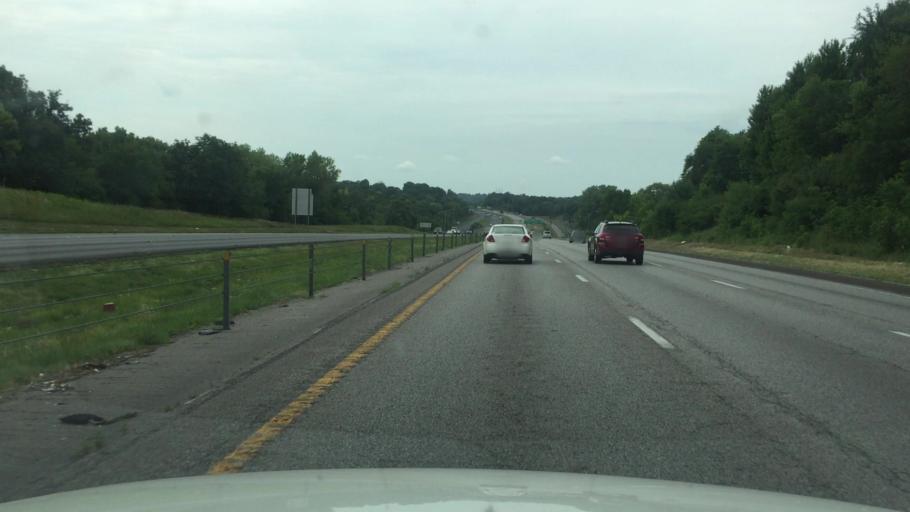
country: US
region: Missouri
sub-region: Jackson County
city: Raytown
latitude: 39.0027
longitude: -94.5020
